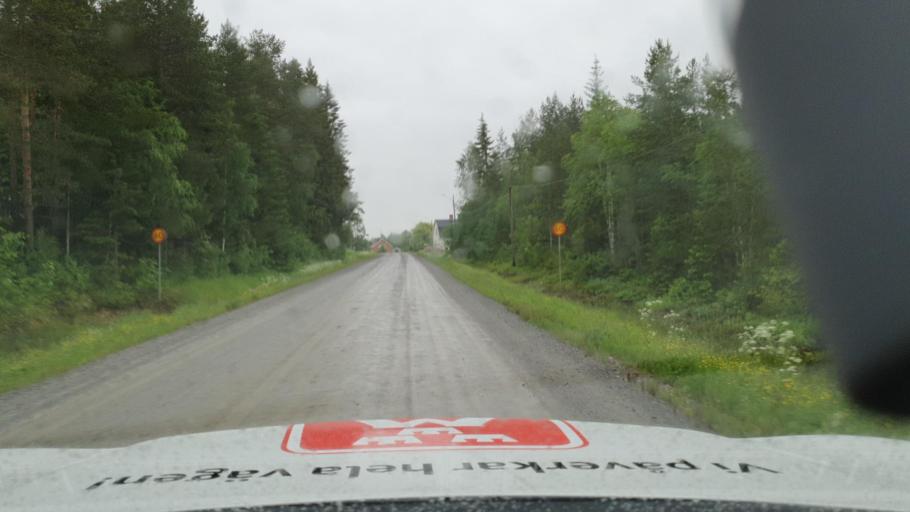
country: SE
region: Vaesterbotten
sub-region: Bjurholms Kommun
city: Bjurholm
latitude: 63.8622
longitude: 19.4675
